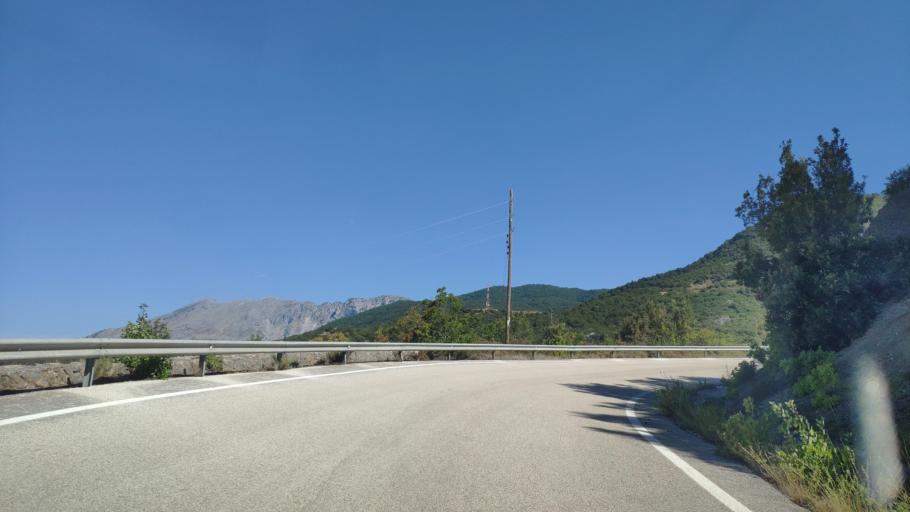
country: GR
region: West Greece
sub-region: Nomos Aitolias kai Akarnanias
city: Sardinia
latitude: 38.9223
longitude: 21.4018
